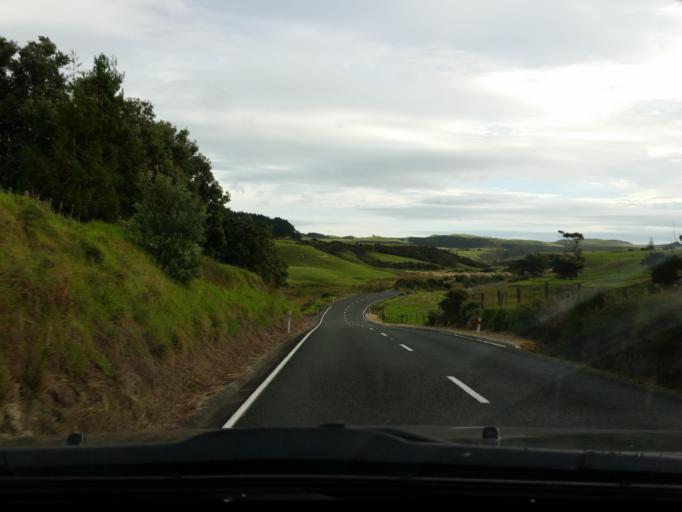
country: NZ
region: Northland
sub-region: Kaipara District
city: Dargaville
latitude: -35.8233
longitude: 173.6804
